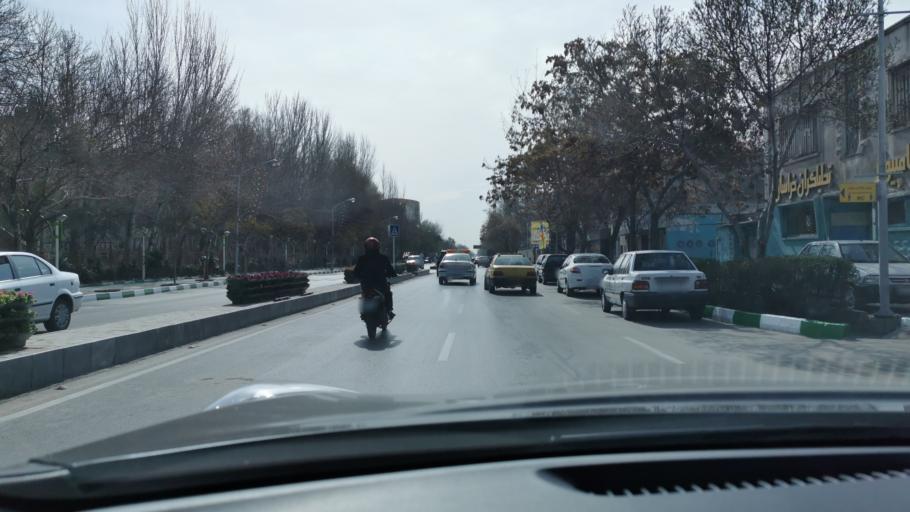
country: IR
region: Razavi Khorasan
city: Mashhad
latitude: 36.2899
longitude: 59.5872
